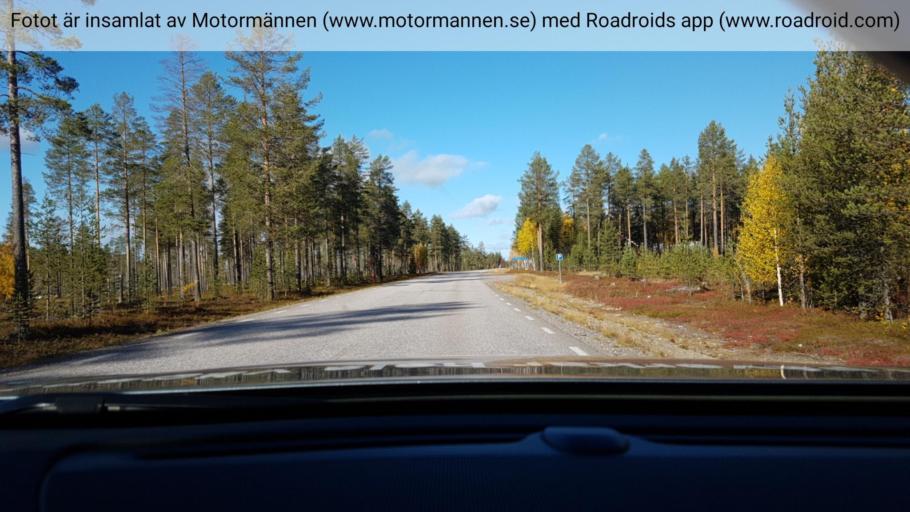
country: SE
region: Norrbotten
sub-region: Arvidsjaurs Kommun
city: Arvidsjaur
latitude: 65.6867
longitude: 18.7924
